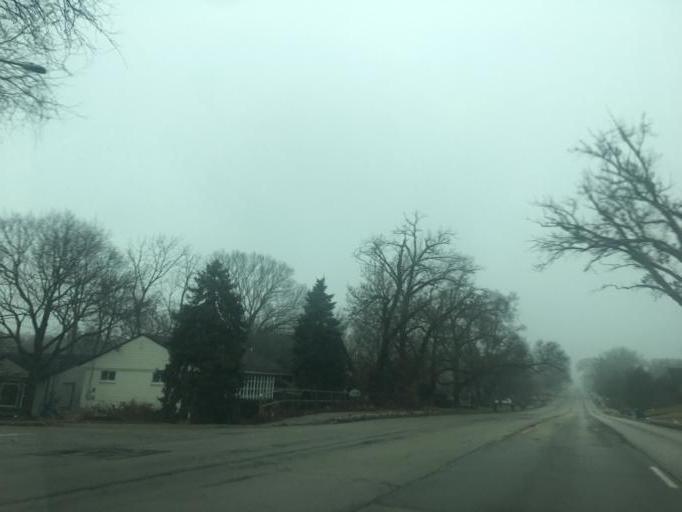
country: US
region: Illinois
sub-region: DuPage County
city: Downers Grove
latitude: 41.7855
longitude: -88.0090
